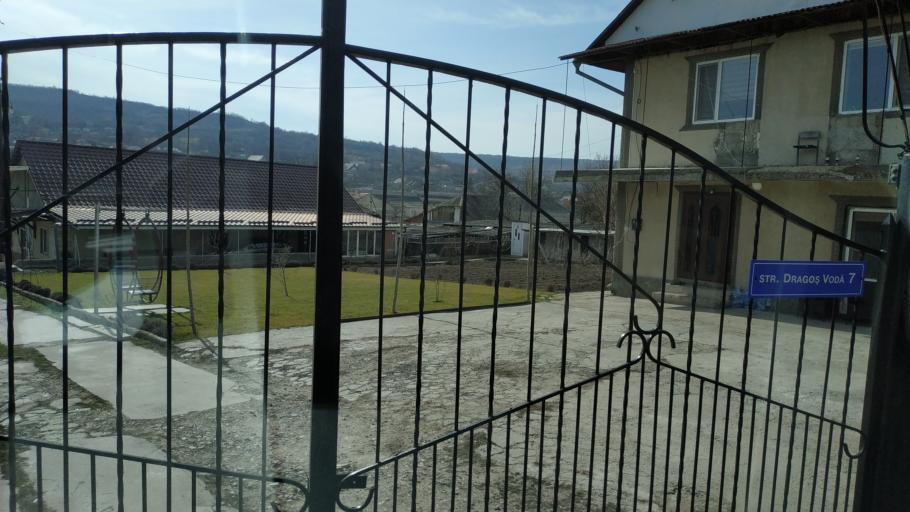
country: MD
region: Straseni
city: Straseni
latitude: 47.0946
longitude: 28.6600
